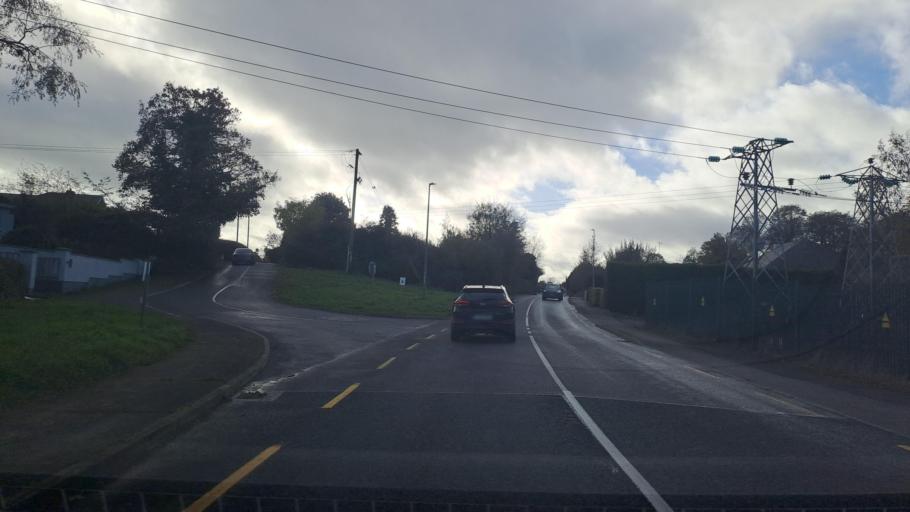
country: IE
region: Ulster
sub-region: County Monaghan
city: Monaghan
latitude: 54.2314
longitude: -6.9688
